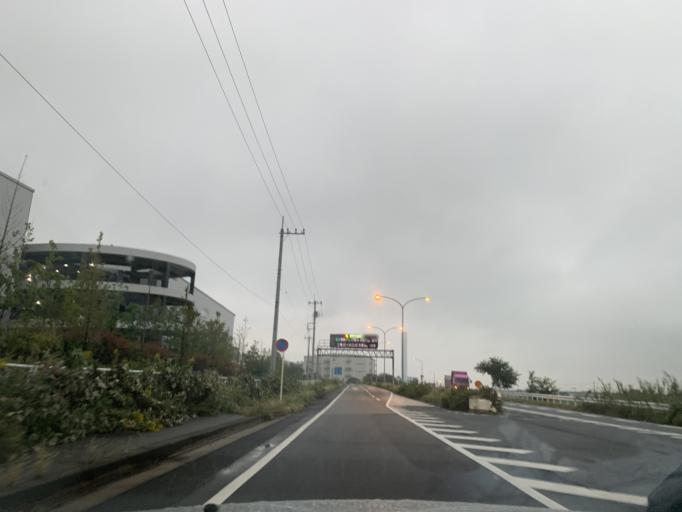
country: JP
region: Chiba
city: Nagareyama
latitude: 35.8865
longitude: 139.8967
